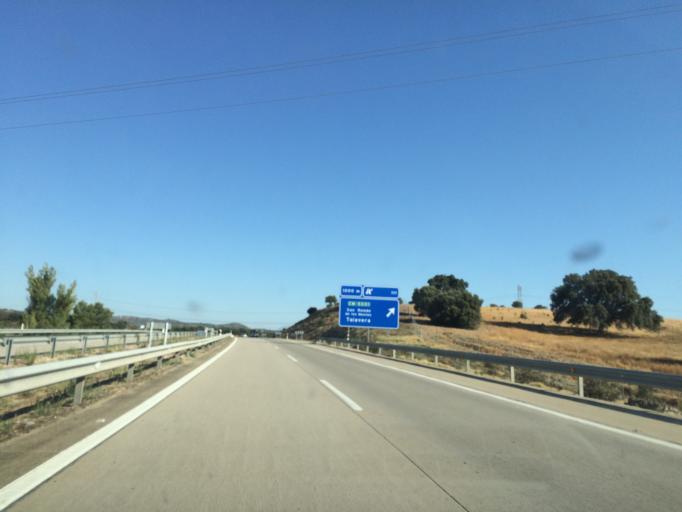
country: ES
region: Castille-La Mancha
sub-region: Province of Toledo
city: Cervera de los Montes
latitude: 40.0041
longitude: -4.7693
